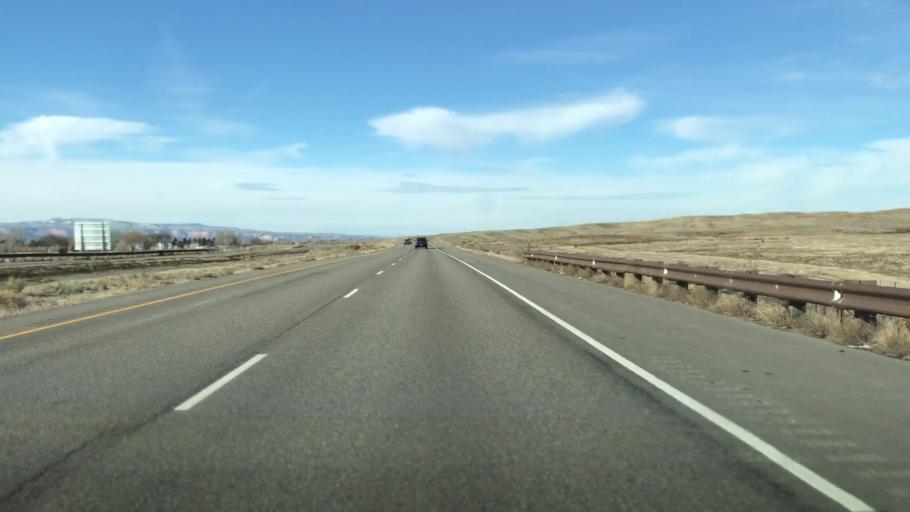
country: US
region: Colorado
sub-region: Mesa County
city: Clifton
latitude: 39.1047
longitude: -108.4681
